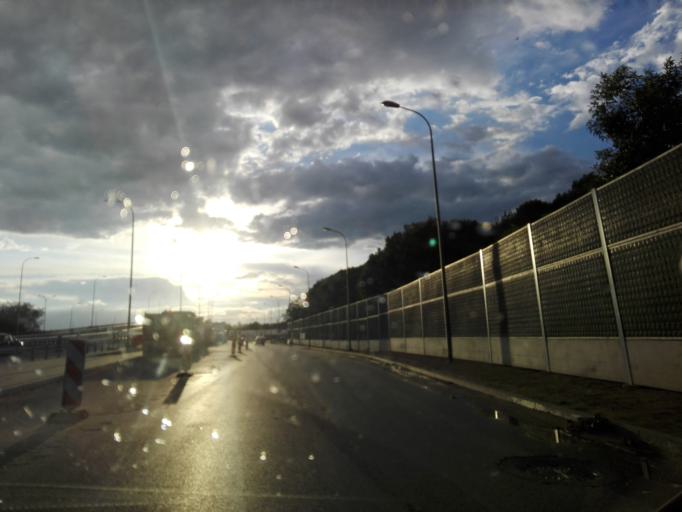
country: PL
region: Lublin Voivodeship
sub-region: Powiat lubelski
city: Lublin
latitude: 51.2577
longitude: 22.5363
